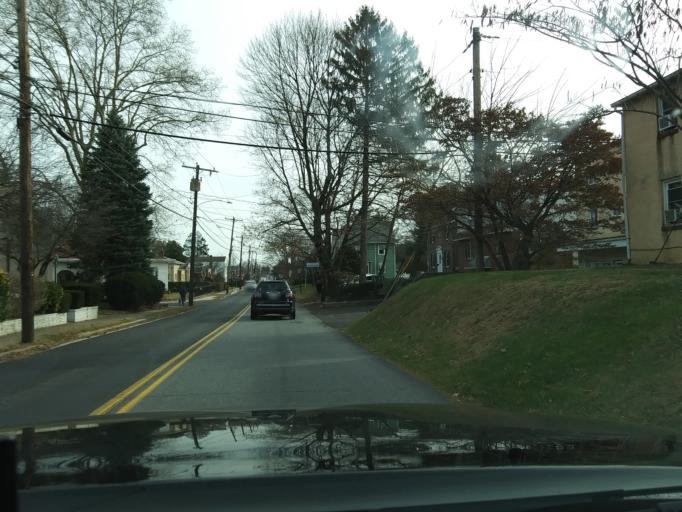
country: US
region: Pennsylvania
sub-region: Montgomery County
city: Rockledge
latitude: 40.0856
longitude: -75.0983
